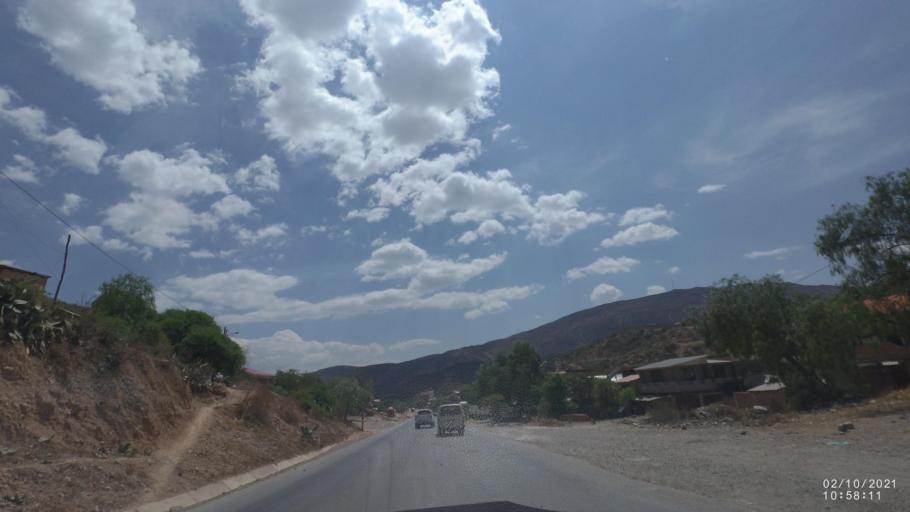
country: BO
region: Cochabamba
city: Sipe Sipe
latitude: -17.5653
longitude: -66.3448
